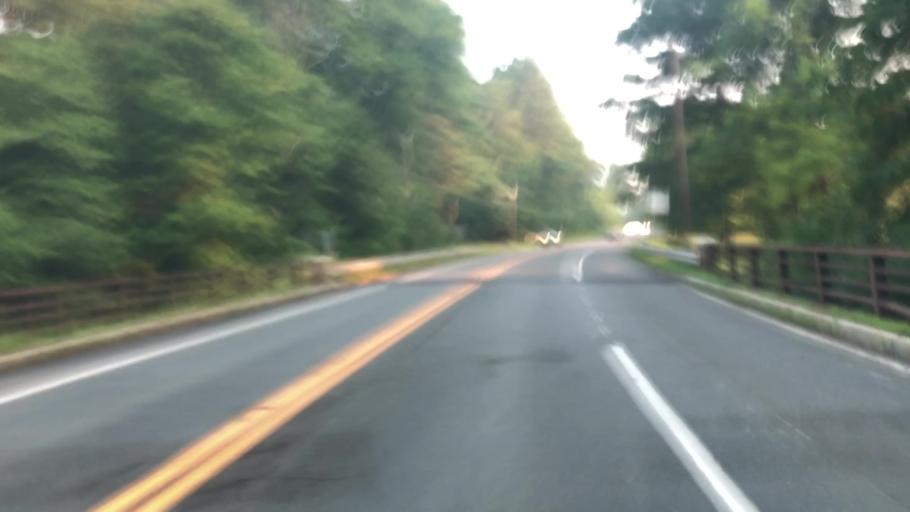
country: US
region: Massachusetts
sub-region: Franklin County
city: Greenfield
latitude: 42.5893
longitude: -72.6310
